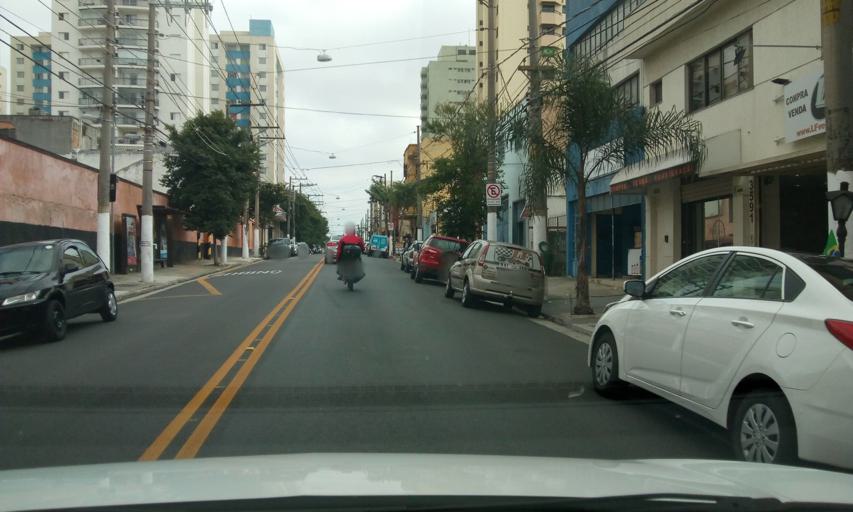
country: BR
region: Sao Paulo
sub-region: Sao Paulo
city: Sao Paulo
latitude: -23.5583
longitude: -46.5906
